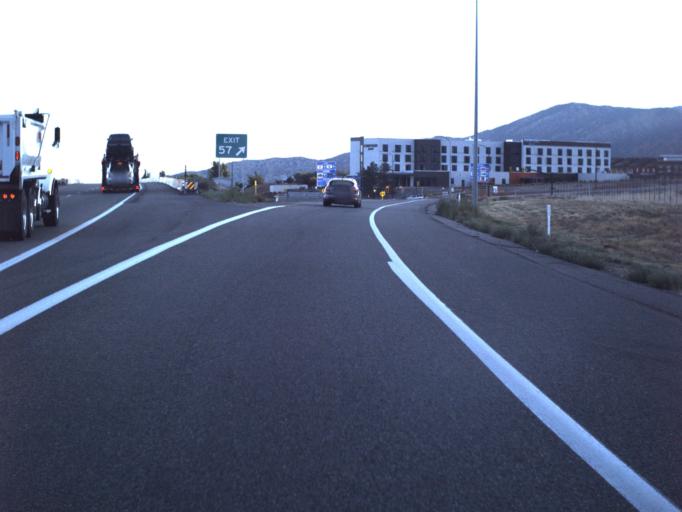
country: US
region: Utah
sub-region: Iron County
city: Cedar City
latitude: 37.6519
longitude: -113.0834
